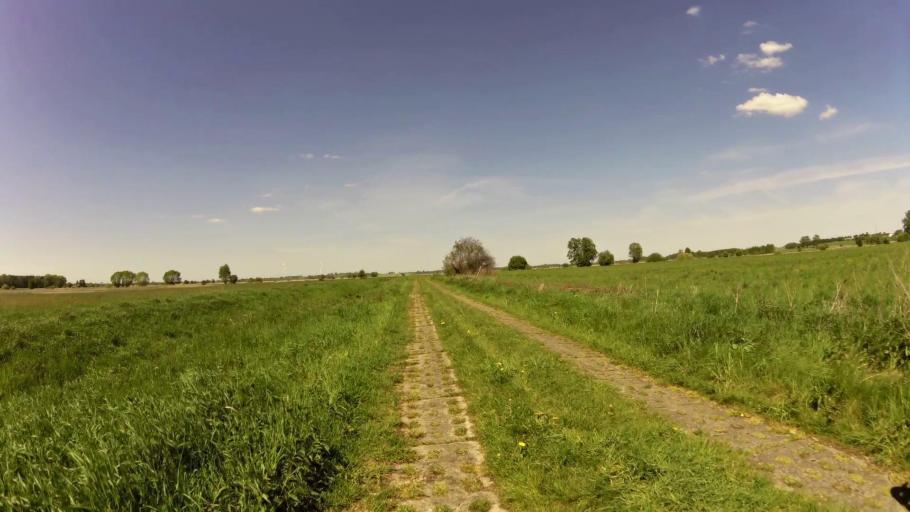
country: PL
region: West Pomeranian Voivodeship
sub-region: Powiat bialogardzki
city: Bialogard
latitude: 53.9980
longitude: 16.0449
